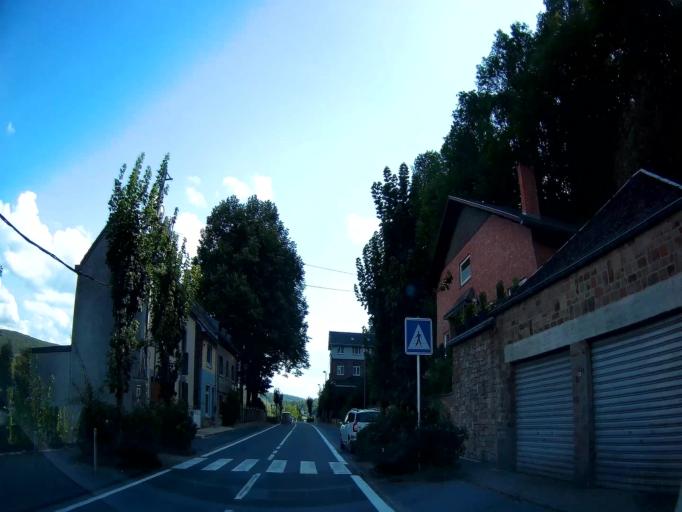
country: BE
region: Wallonia
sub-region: Province de Namur
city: Profondeville
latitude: 50.3456
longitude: 4.8536
